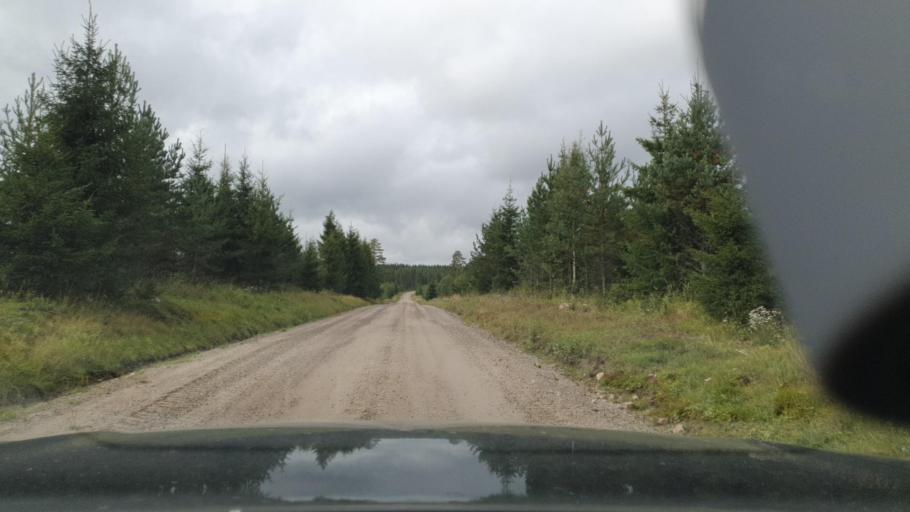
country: NO
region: Hedmark
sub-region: Trysil
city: Innbygda
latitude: 60.9418
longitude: 12.4534
